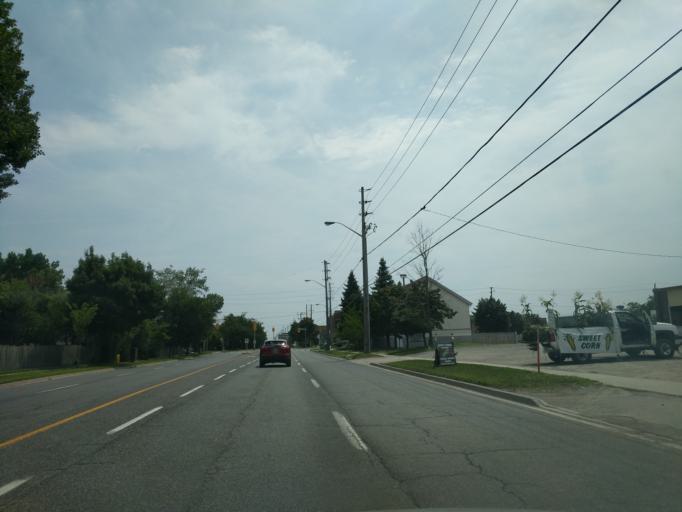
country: CA
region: Ontario
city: Markham
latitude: 43.8218
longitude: -79.2954
